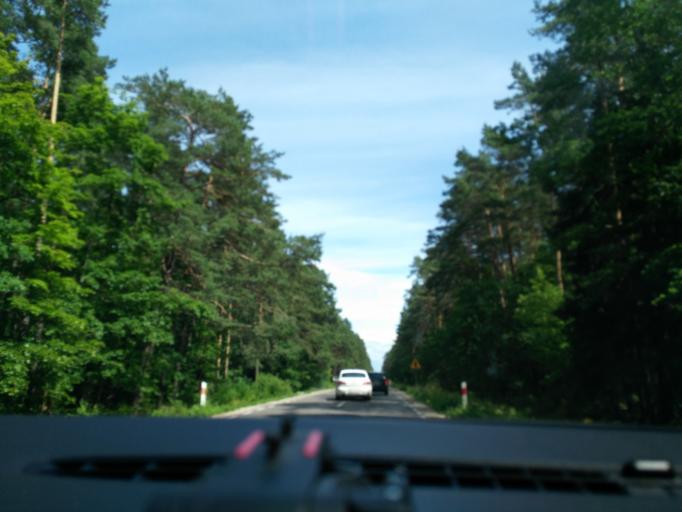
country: PL
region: Podlasie
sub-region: Powiat augustowski
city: Augustow
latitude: 53.8470
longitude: 23.0087
